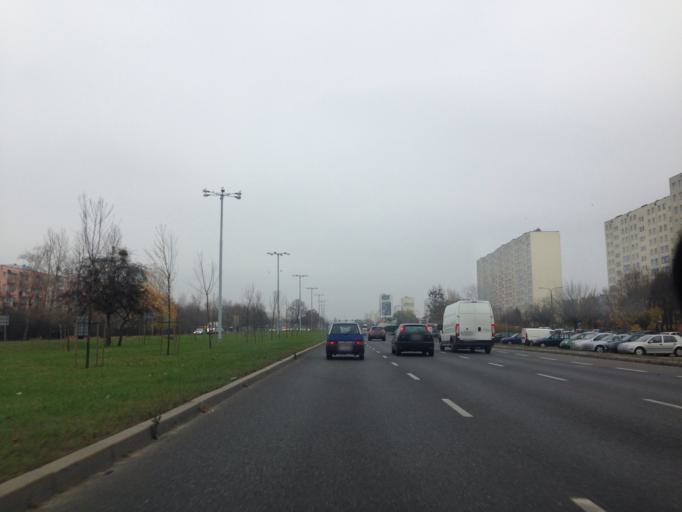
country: PL
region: Kujawsko-Pomorskie
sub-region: Powiat torunski
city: Lubicz Dolny
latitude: 53.0257
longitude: 18.6746
